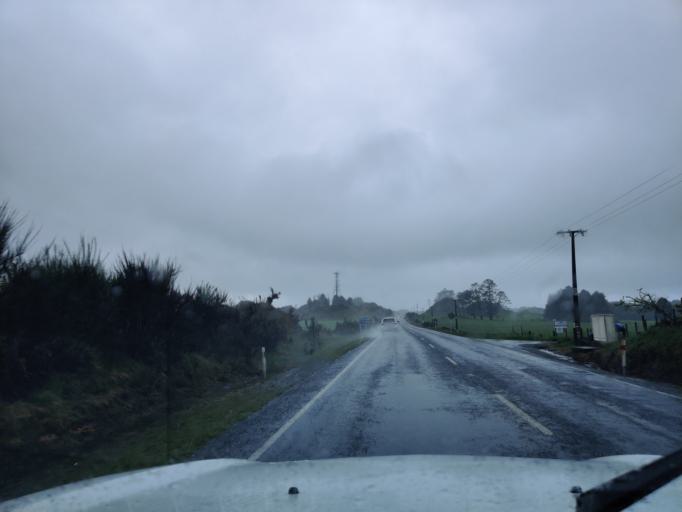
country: NZ
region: Bay of Plenty
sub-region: Rotorua District
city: Rotorua
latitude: -38.0406
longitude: 176.0568
